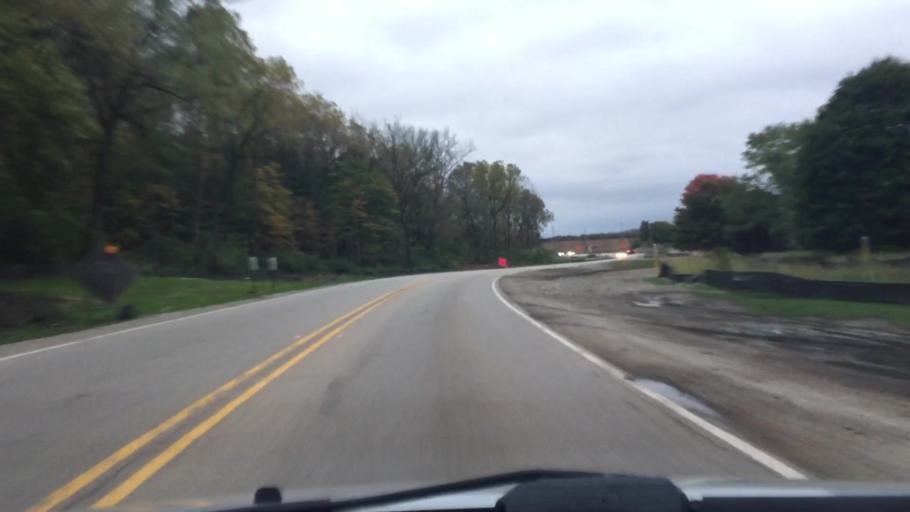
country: US
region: Illinois
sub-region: McHenry County
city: Algonquin
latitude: 42.1346
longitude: -88.2990
